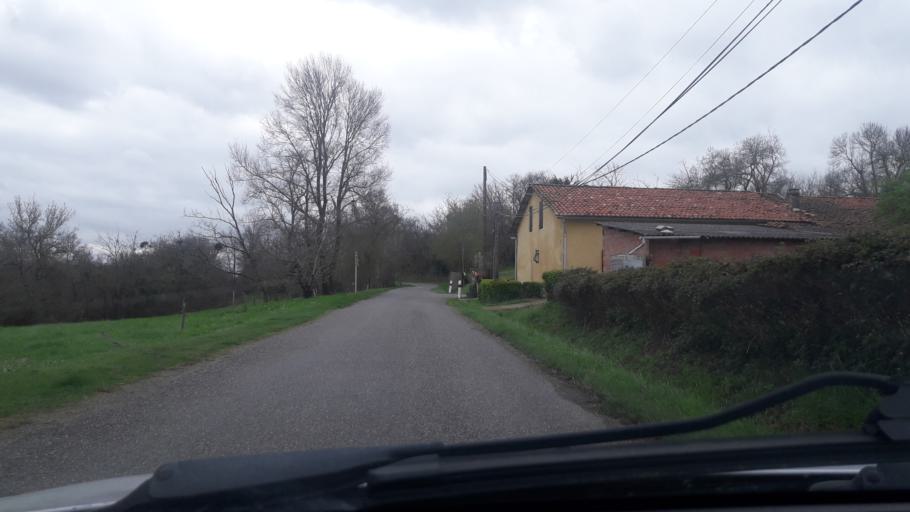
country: FR
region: Midi-Pyrenees
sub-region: Departement de l'Ariege
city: Lezat-sur-Leze
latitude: 43.1796
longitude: 1.3321
